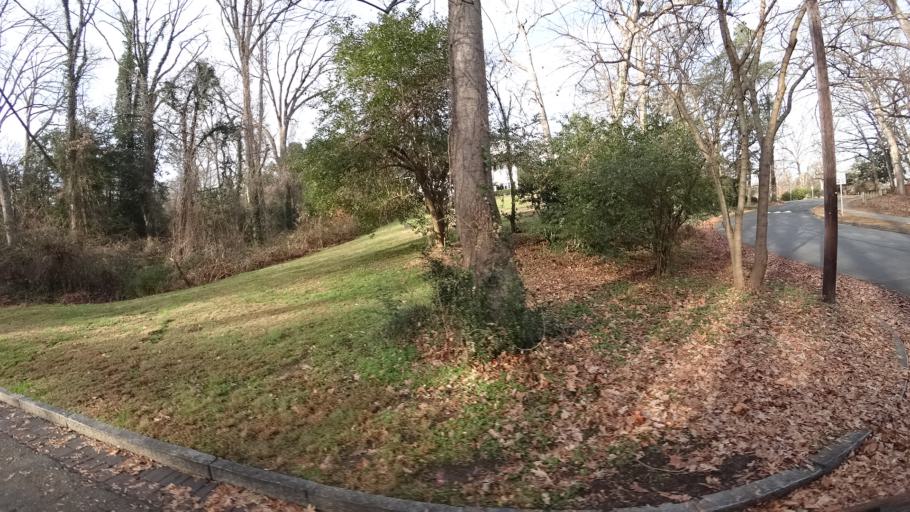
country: US
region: North Carolina
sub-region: Durham County
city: Durham
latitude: 36.0121
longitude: -78.8925
